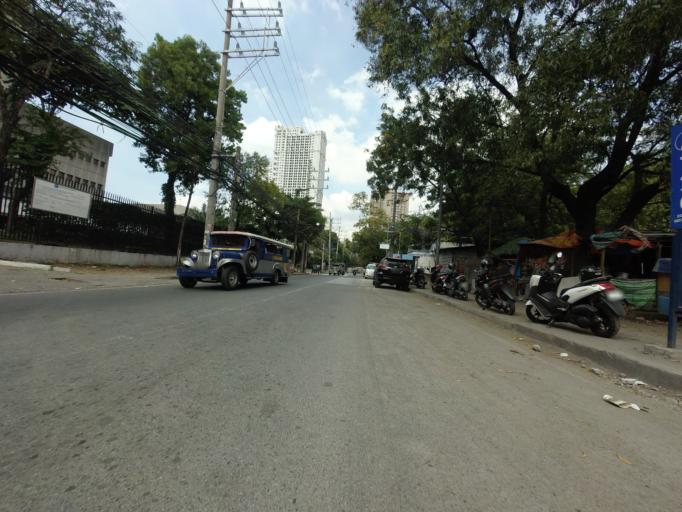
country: PH
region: Metro Manila
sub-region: City of Manila
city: Port Area
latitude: 14.5630
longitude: 120.9880
